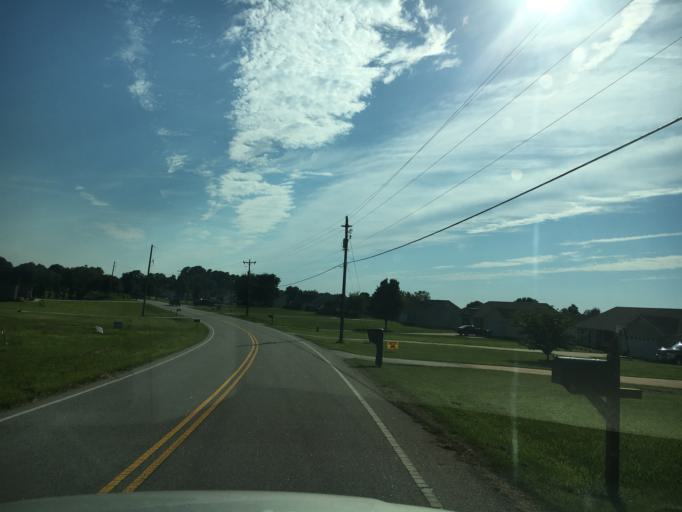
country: US
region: South Carolina
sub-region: Spartanburg County
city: Boiling Springs
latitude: 35.0864
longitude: -81.9338
